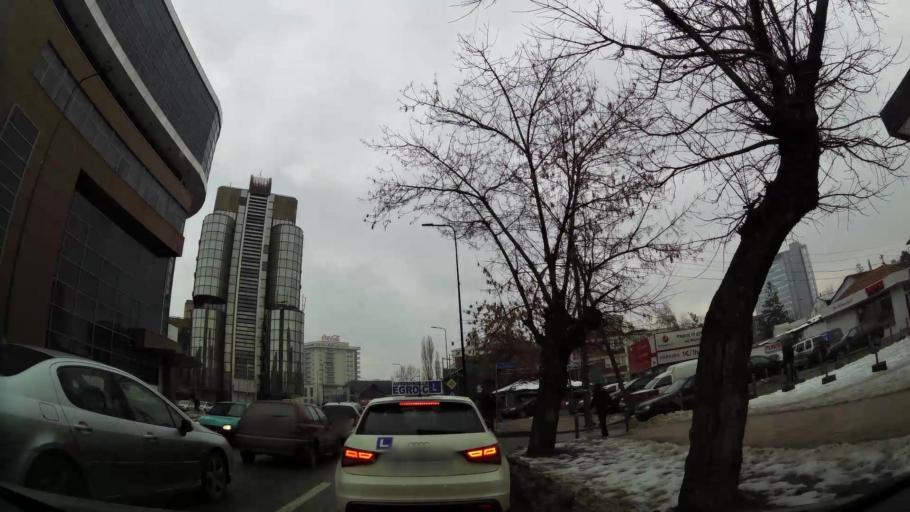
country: XK
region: Pristina
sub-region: Komuna e Prishtines
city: Pristina
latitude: 42.6633
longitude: 21.1604
